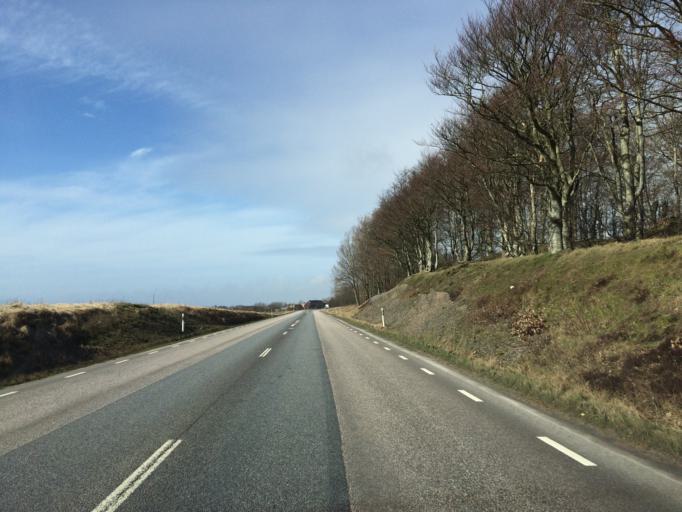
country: SE
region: Halland
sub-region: Halmstads Kommun
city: Paarp
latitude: 56.6023
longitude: 12.9651
